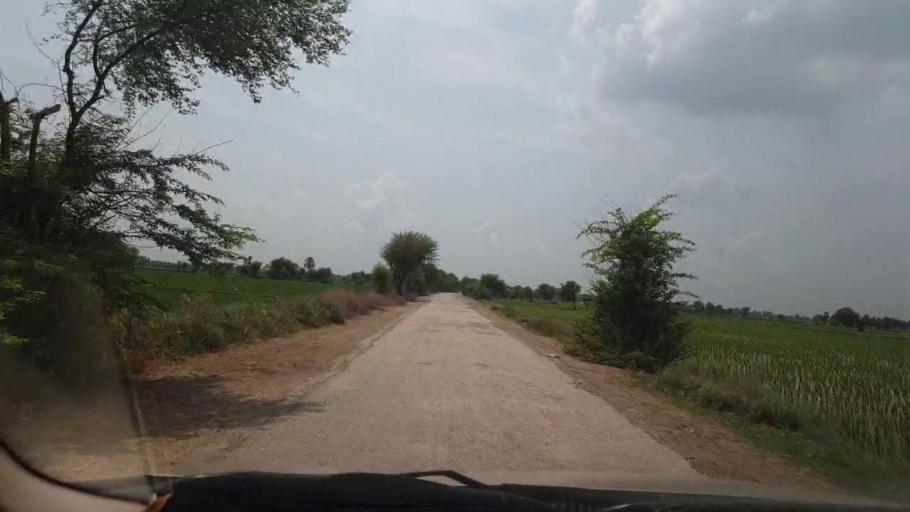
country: PK
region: Sindh
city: Larkana
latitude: 27.6128
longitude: 68.1352
